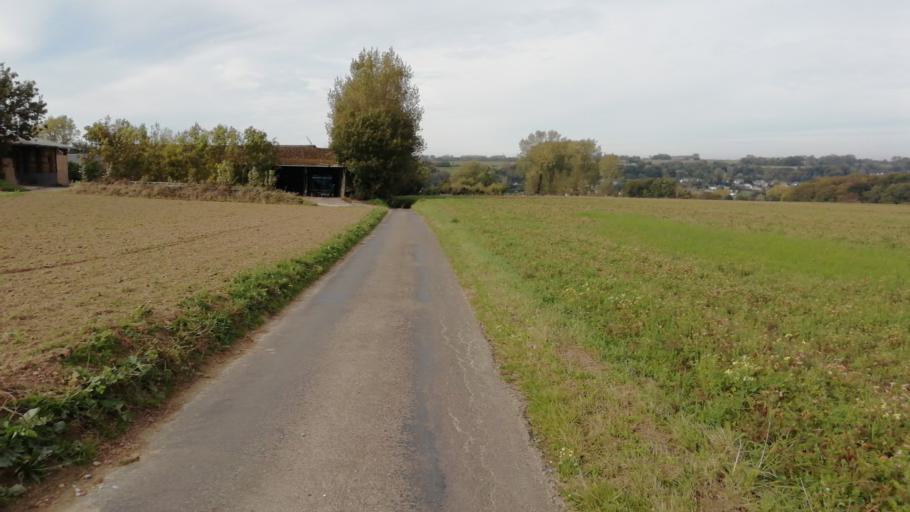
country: FR
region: Haute-Normandie
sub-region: Departement de la Seine-Maritime
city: Epouville
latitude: 49.5436
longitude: 0.2123
